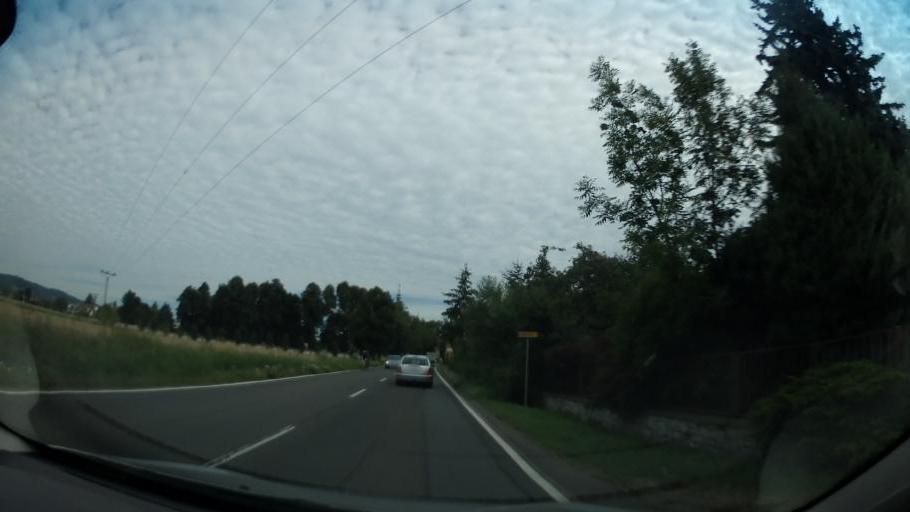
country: CZ
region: Olomoucky
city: Postrelmov
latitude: 49.9044
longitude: 16.9109
